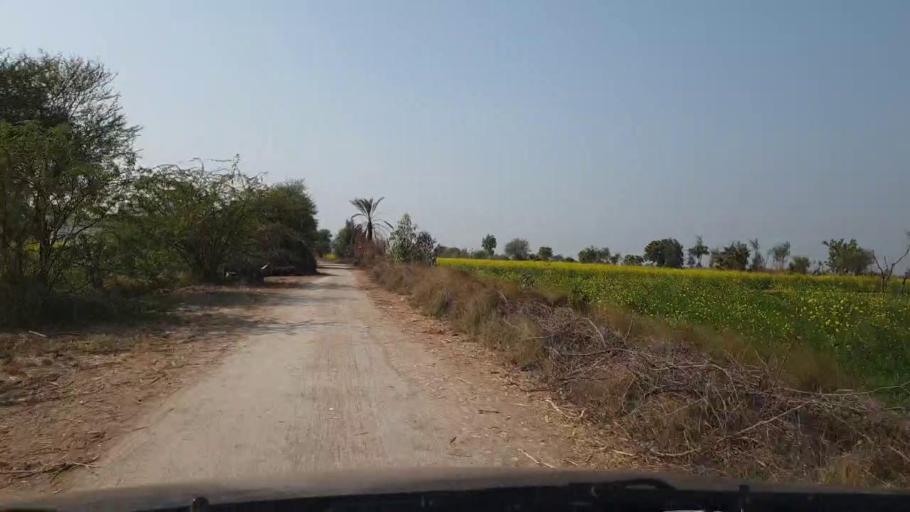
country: PK
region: Sindh
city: Sanghar
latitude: 26.0191
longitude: 68.9082
